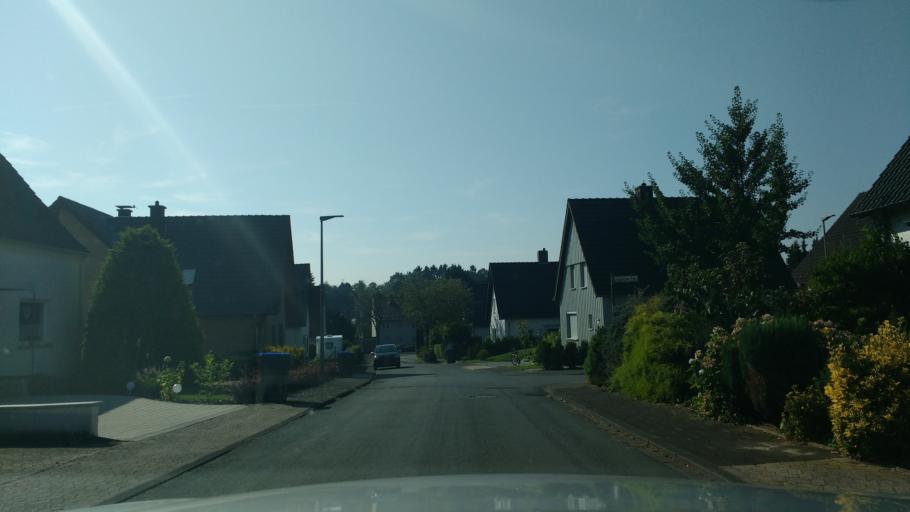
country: DE
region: North Rhine-Westphalia
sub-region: Regierungsbezirk Detmold
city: Lemgo
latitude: 52.0284
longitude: 8.9244
